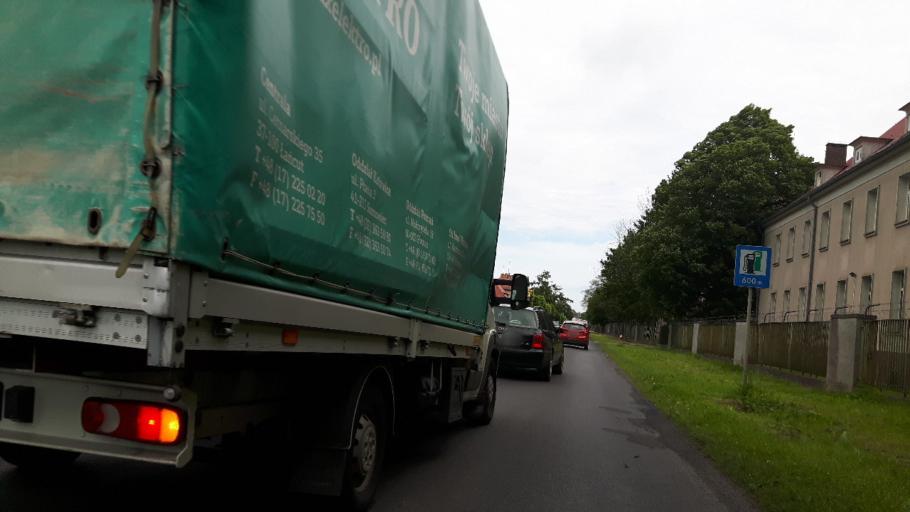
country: PL
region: West Pomeranian Voivodeship
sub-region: Powiat gryficki
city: Trzebiatow
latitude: 54.0515
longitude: 15.2561
